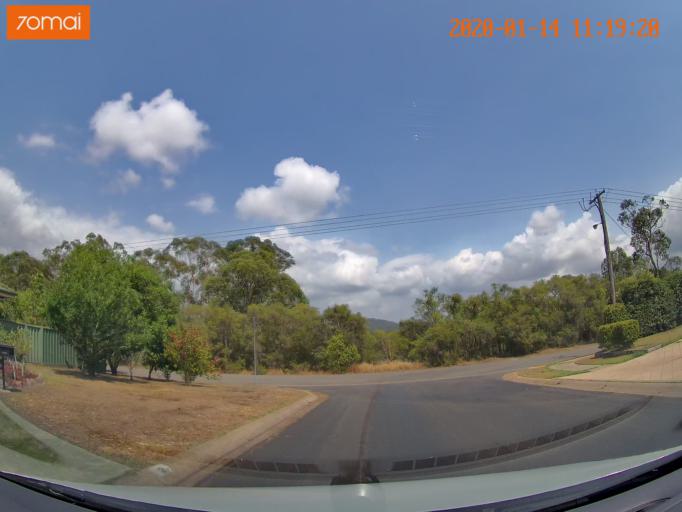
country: AU
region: New South Wales
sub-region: Lake Macquarie Shire
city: Cooranbong
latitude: -33.0978
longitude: 151.4608
